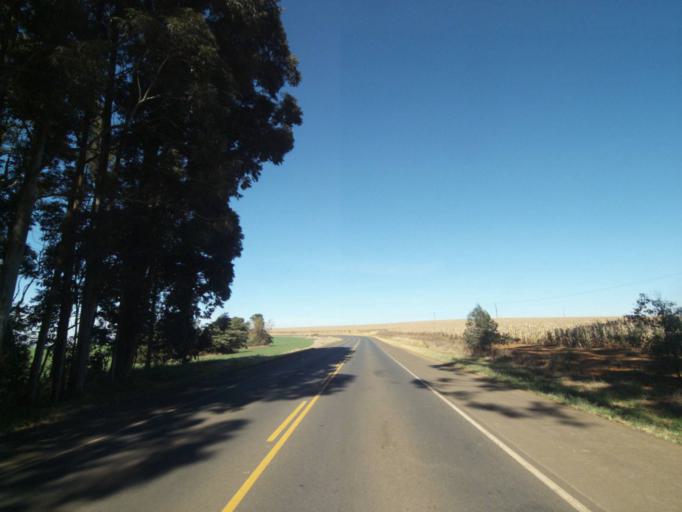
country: BR
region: Parana
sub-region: Tibagi
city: Tibagi
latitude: -24.3898
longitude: -50.3355
